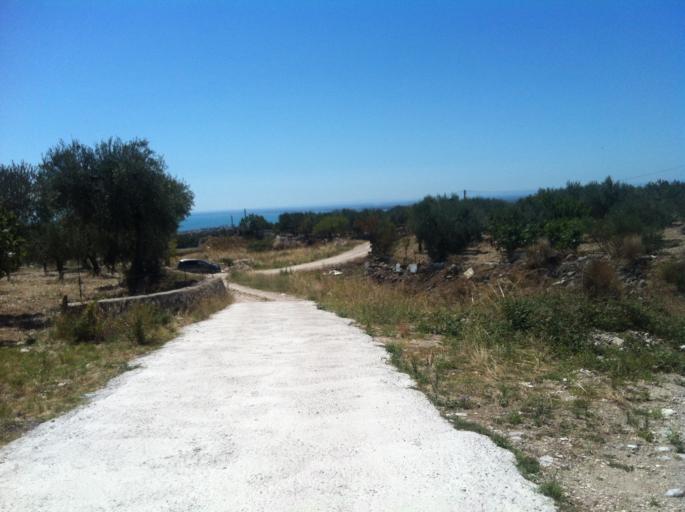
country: IT
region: Apulia
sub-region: Provincia di Foggia
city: Manfredonia
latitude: 41.6593
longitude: 15.9136
